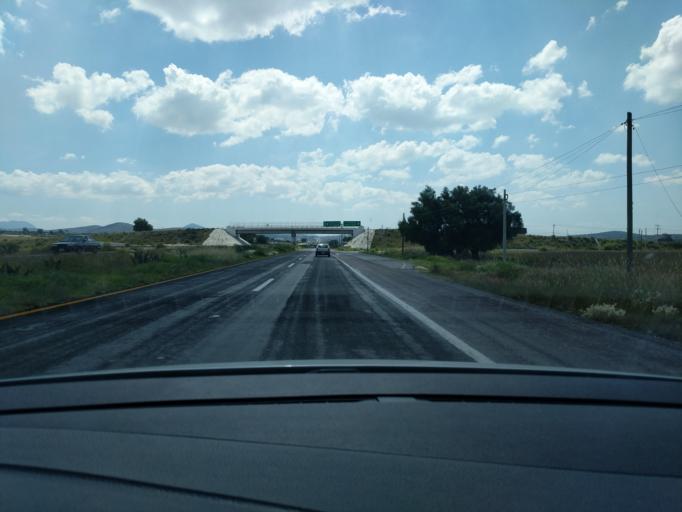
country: MX
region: Hidalgo
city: Zempoala
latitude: 19.9602
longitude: -98.6948
